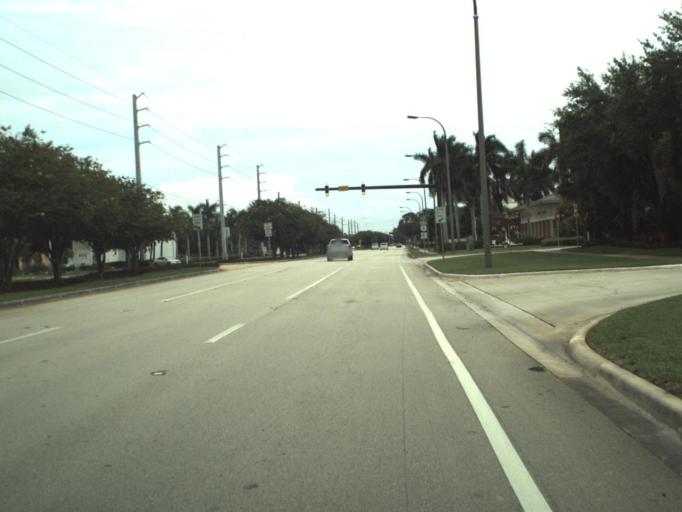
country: US
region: Florida
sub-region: Palm Beach County
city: Lake Park
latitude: 26.8113
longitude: -80.0566
